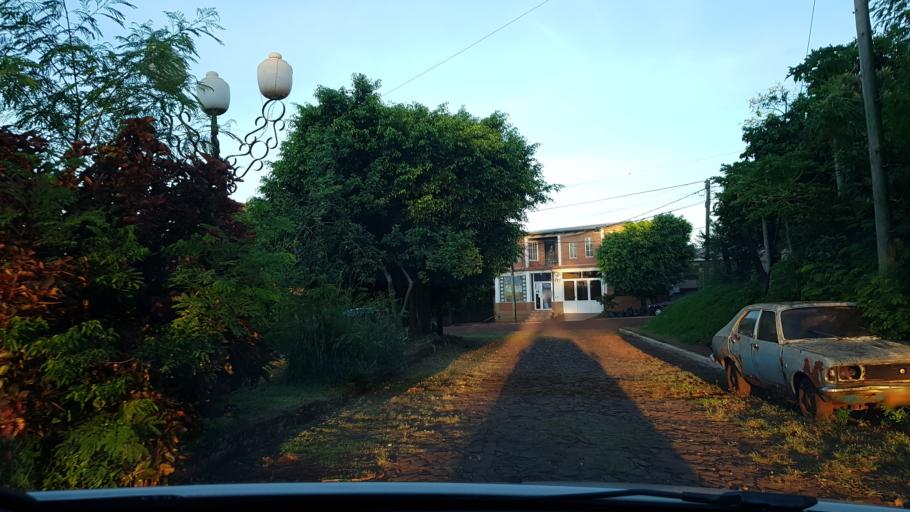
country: AR
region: Misiones
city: Puerto Libertad
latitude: -25.9228
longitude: -54.5802
